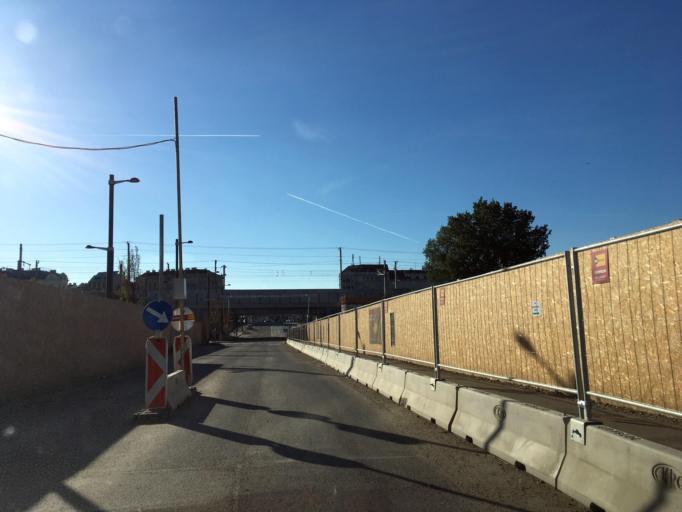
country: AT
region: Vienna
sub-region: Wien Stadt
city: Vienna
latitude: 48.2281
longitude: 16.3917
